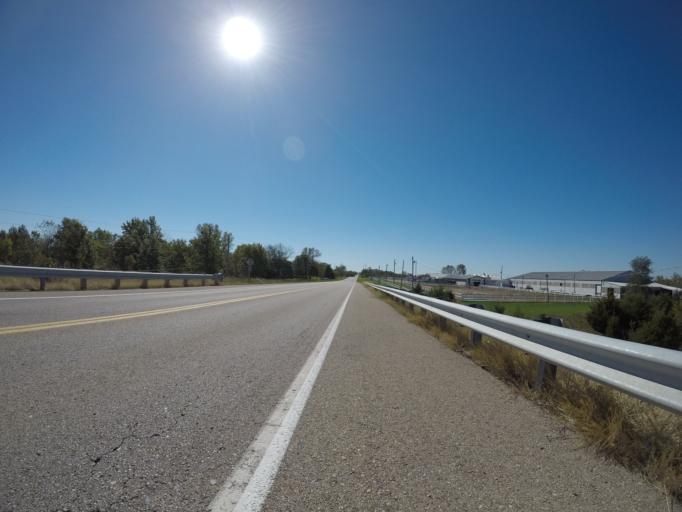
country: US
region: Kansas
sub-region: Leavenworth County
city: Basehor
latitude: 39.0824
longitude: -94.9458
